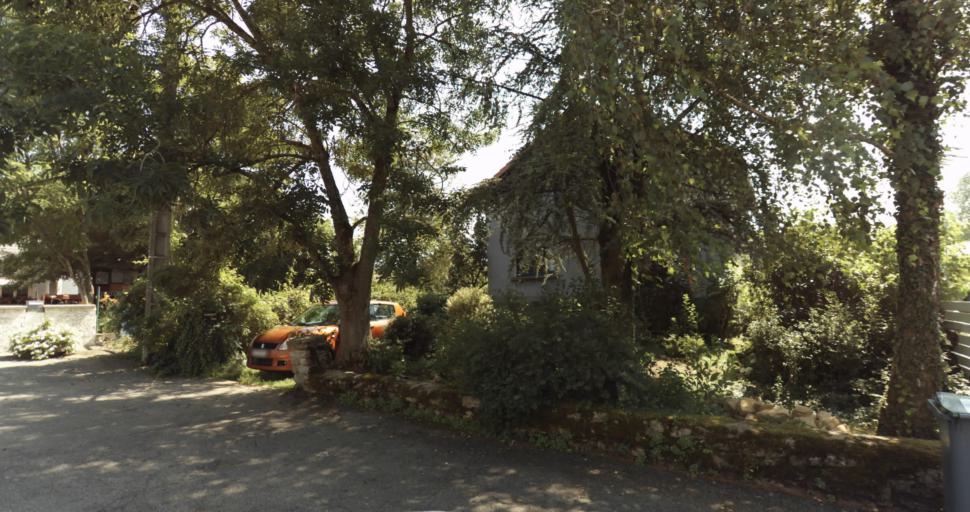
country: FR
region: Lorraine
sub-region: Departement de Meurthe-et-Moselle
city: Briey
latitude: 49.2666
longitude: 5.9171
